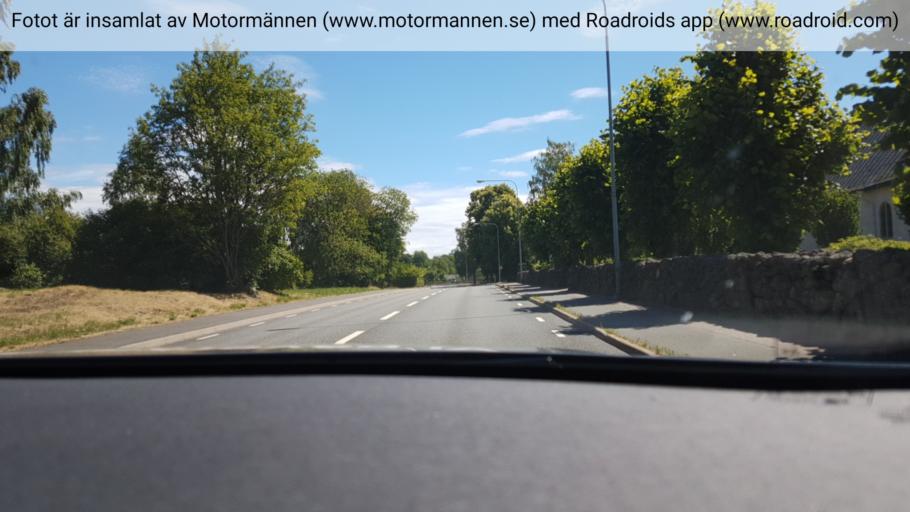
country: SE
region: Joenkoeping
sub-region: Jonkopings Kommun
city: Asa
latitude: 58.0078
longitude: 14.5722
